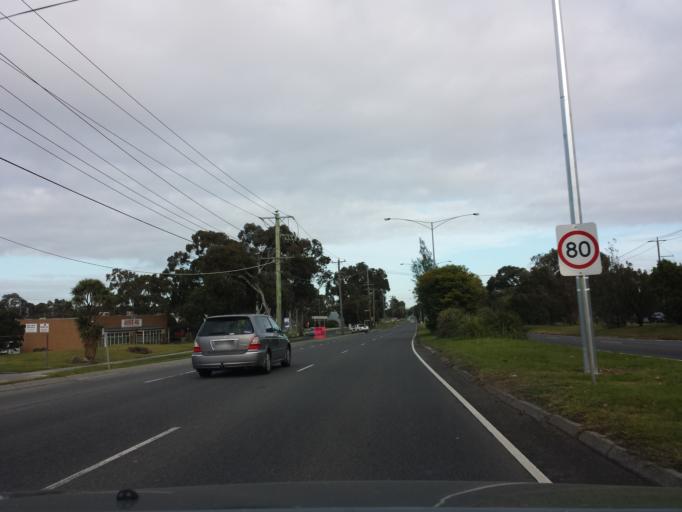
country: AU
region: Victoria
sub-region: Knox
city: Knoxfield
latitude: -37.8926
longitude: 145.2562
